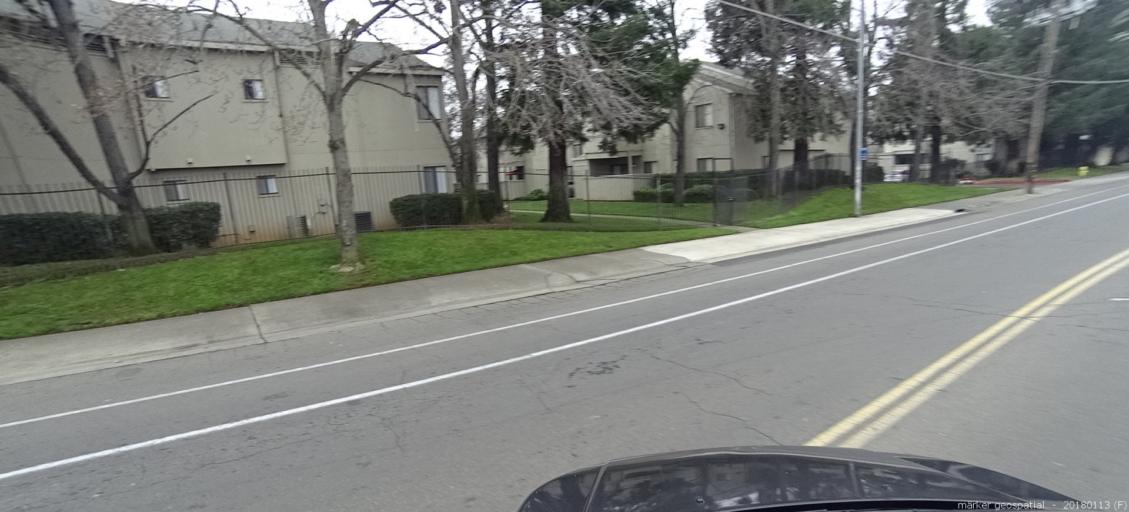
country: US
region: California
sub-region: Sacramento County
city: Rancho Cordova
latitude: 38.6000
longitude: -121.2826
